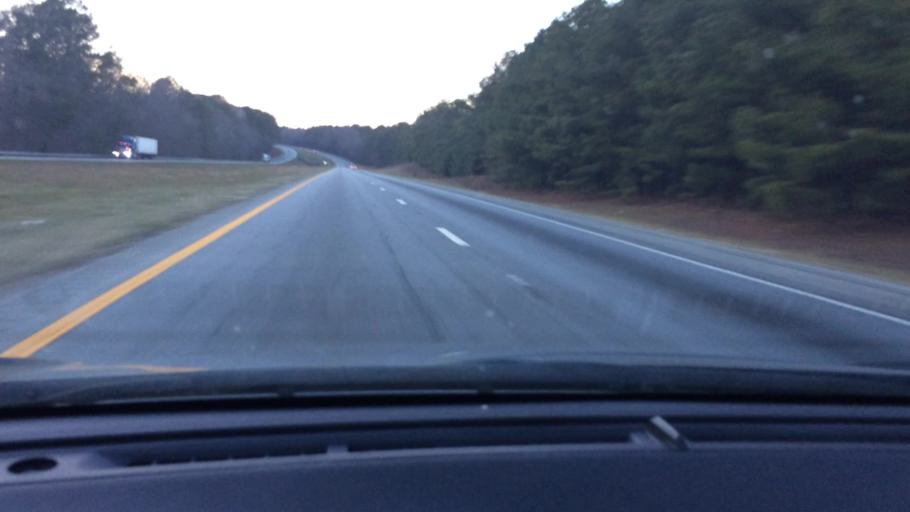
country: US
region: South Carolina
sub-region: Laurens County
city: Joanna
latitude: 34.4197
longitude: -81.7140
